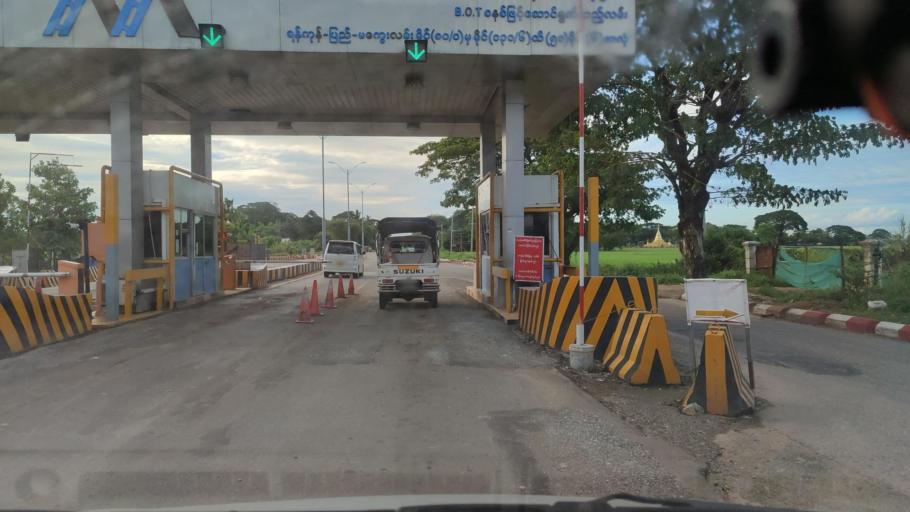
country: MM
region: Bago
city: Tharyarwady
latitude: 17.6991
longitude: 95.7817
